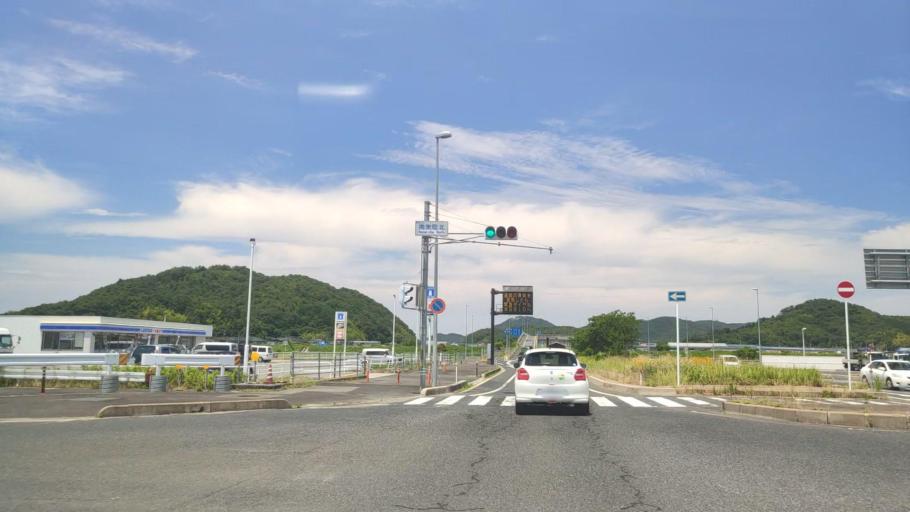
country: JP
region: Tottori
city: Tottori
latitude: 35.4619
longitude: 134.2430
